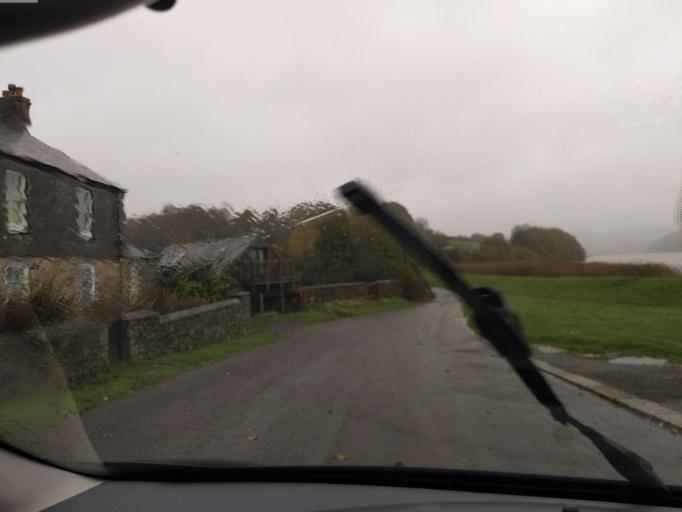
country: GB
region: England
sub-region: Devon
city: Bere Alston
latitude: 50.4682
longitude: -4.2367
